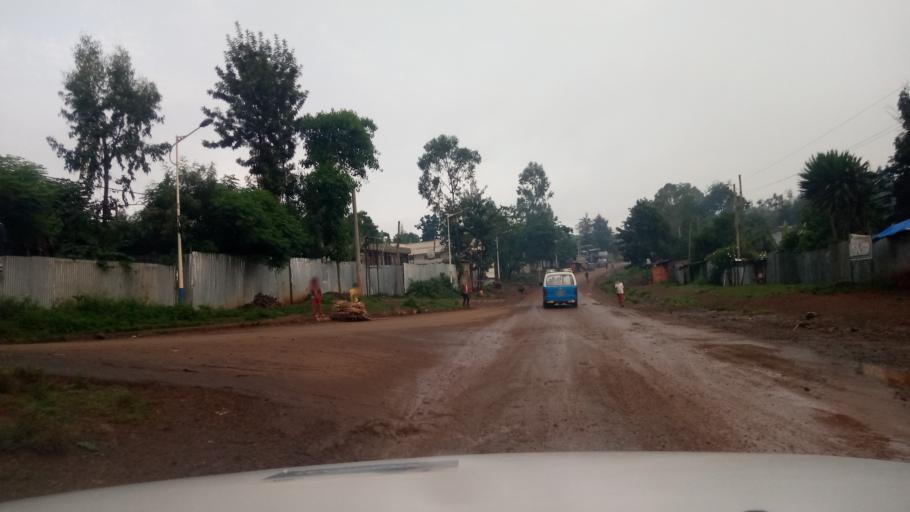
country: ET
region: Oromiya
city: Jima
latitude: 7.6941
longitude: 36.8191
